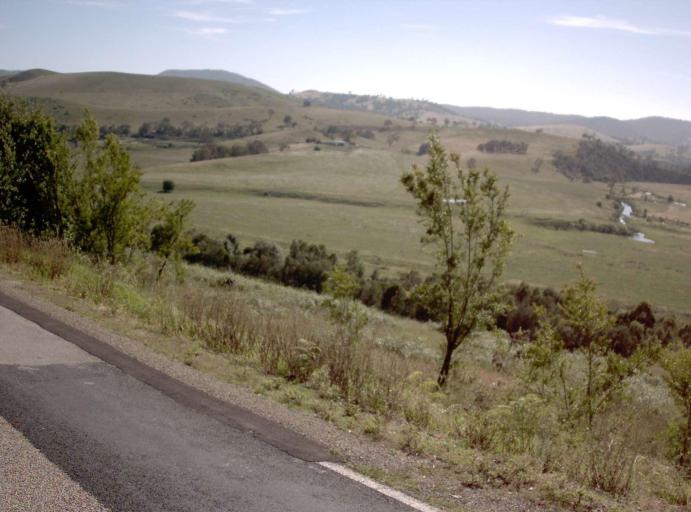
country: AU
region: Victoria
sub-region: East Gippsland
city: Lakes Entrance
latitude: -37.5081
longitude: 148.1708
